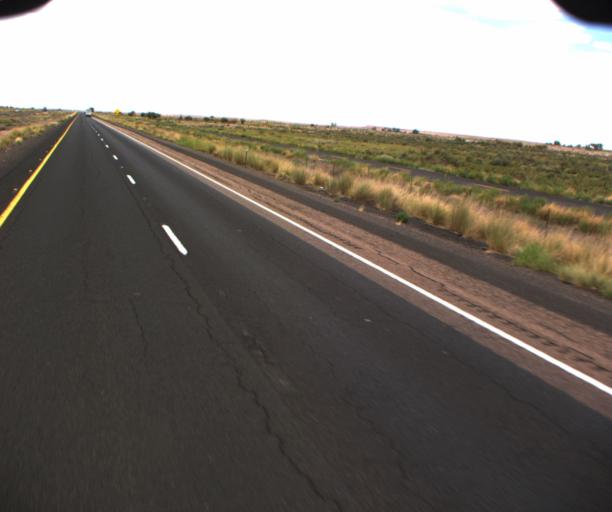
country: US
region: Arizona
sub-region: Navajo County
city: Joseph City
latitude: 34.9605
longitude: -110.3775
